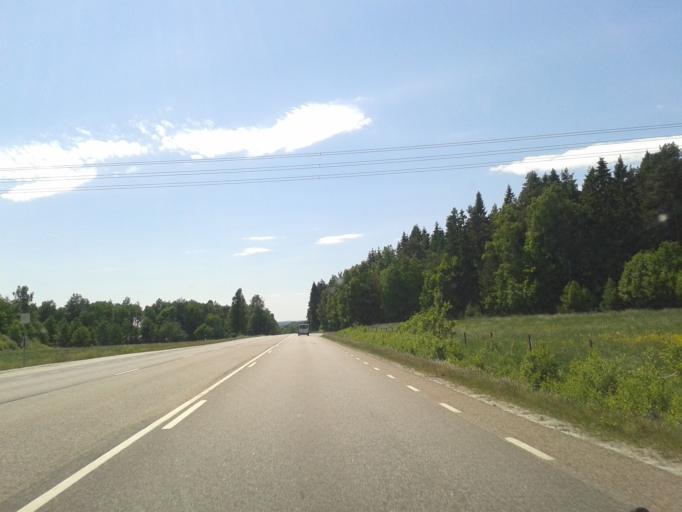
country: SE
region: Vaestra Goetaland
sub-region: Stenungsunds Kommun
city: Stora Hoga
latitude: 58.0523
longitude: 11.9045
